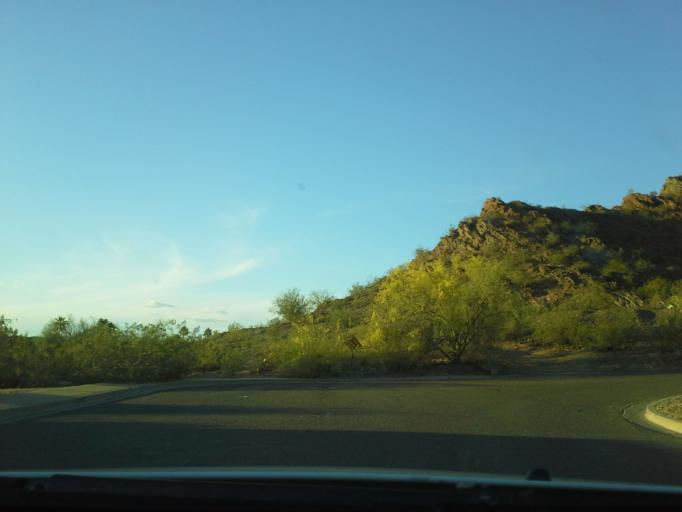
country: US
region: Arizona
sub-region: Maricopa County
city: Paradise Valley
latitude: 33.5773
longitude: -112.0479
